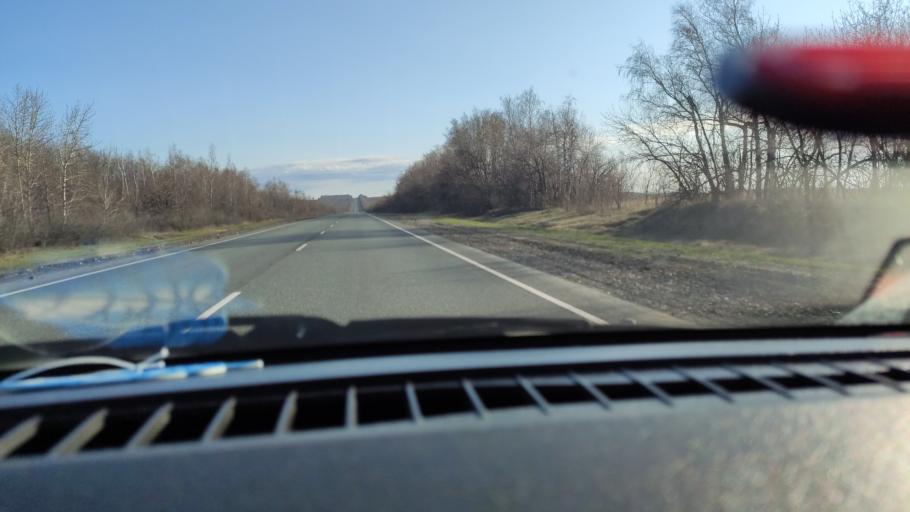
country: RU
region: Saratov
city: Khvalynsk
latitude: 52.6019
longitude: 48.1462
